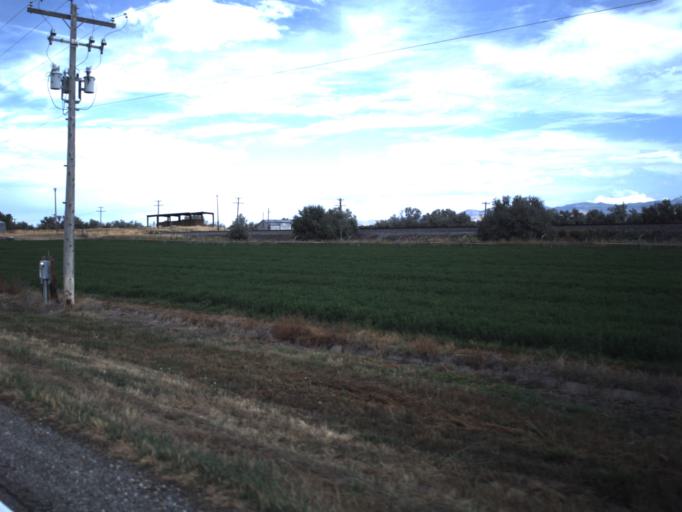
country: US
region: Utah
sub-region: Cache County
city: Lewiston
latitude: 41.9839
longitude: -111.9545
